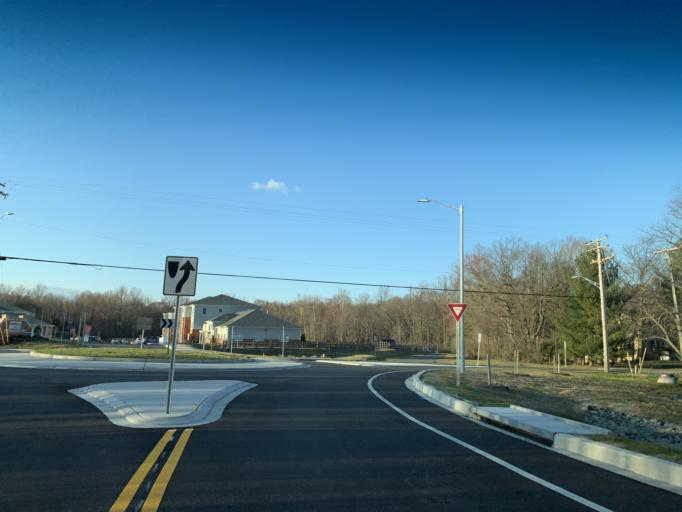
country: US
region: Maryland
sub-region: Harford County
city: Aberdeen
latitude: 39.5269
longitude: -76.1776
